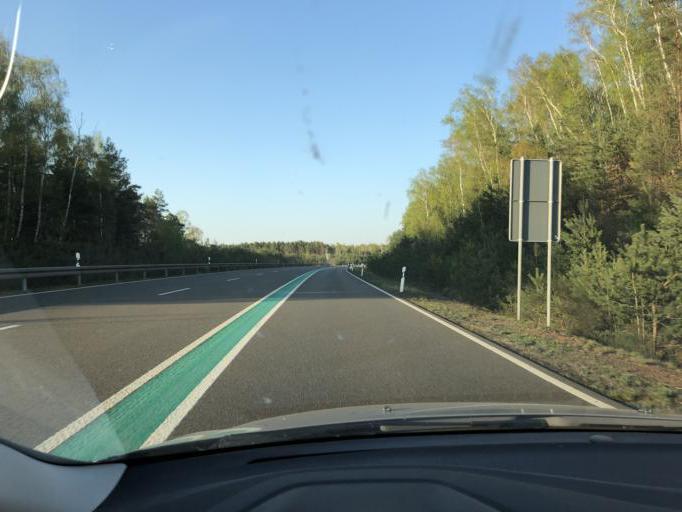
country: DE
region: Brandenburg
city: Schwarzbach
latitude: 51.4927
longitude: 13.9425
